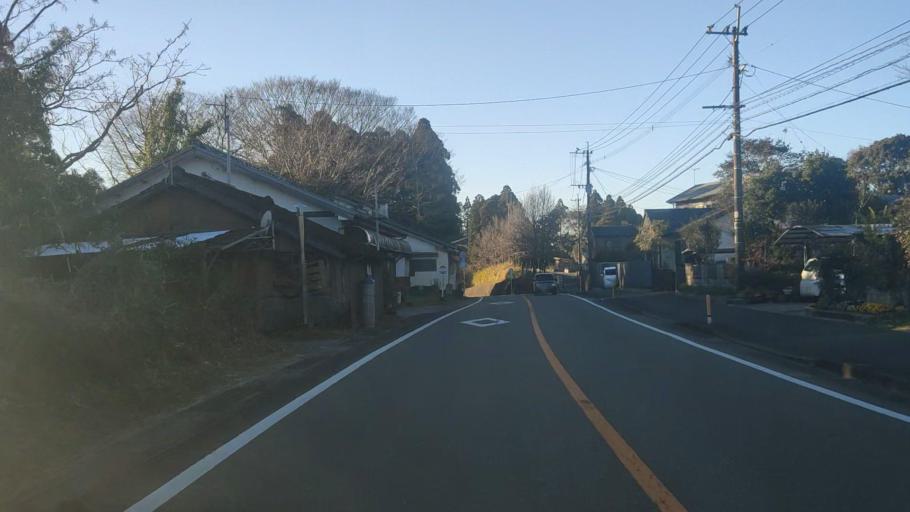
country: JP
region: Miyazaki
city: Miyazaki-shi
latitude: 31.8588
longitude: 131.3752
